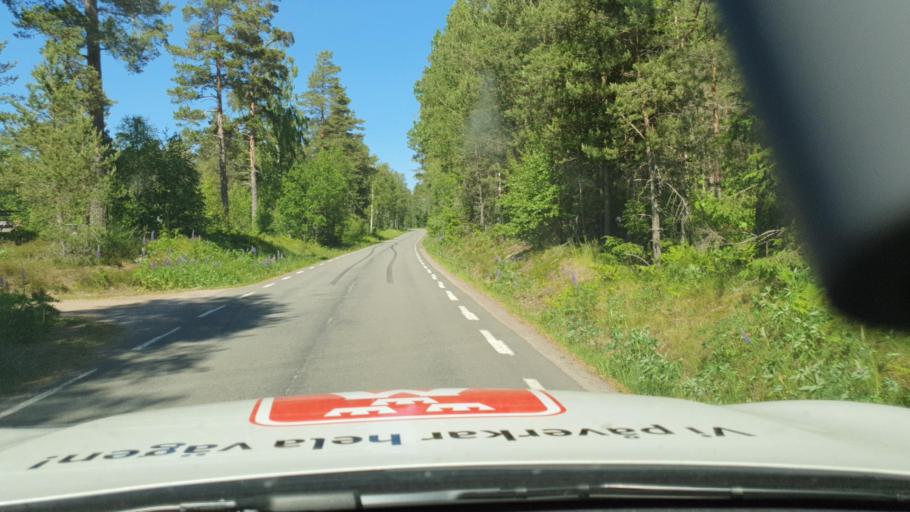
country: SE
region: Vaestra Goetaland
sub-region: Tidaholms Kommun
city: Tidaholm
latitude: 58.0938
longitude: 14.0747
